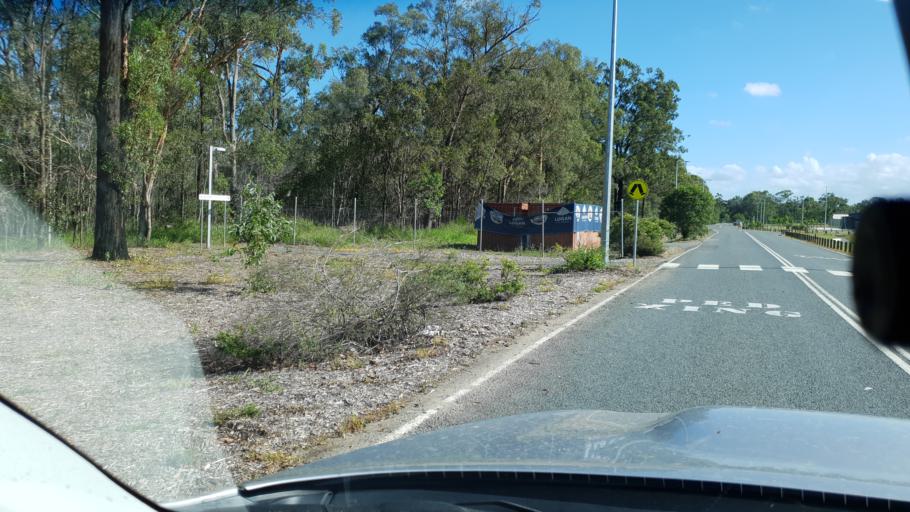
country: AU
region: Queensland
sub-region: Logan
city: Woodridge
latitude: -27.6705
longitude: 153.0707
